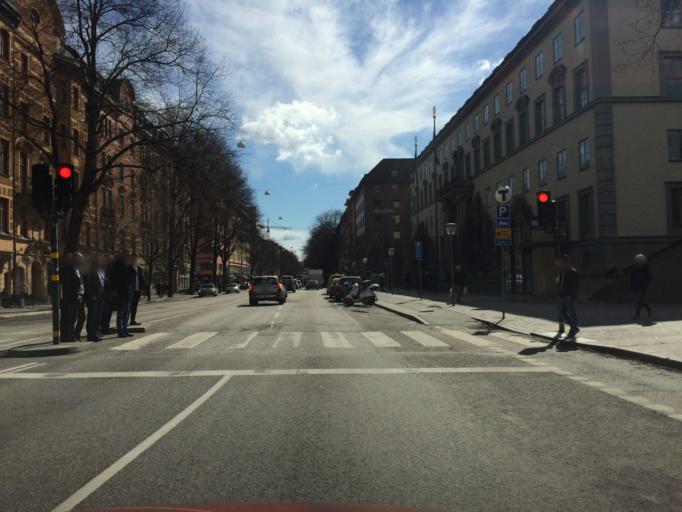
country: SE
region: Stockholm
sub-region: Stockholms Kommun
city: Stockholm
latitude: 59.3424
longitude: 18.0570
